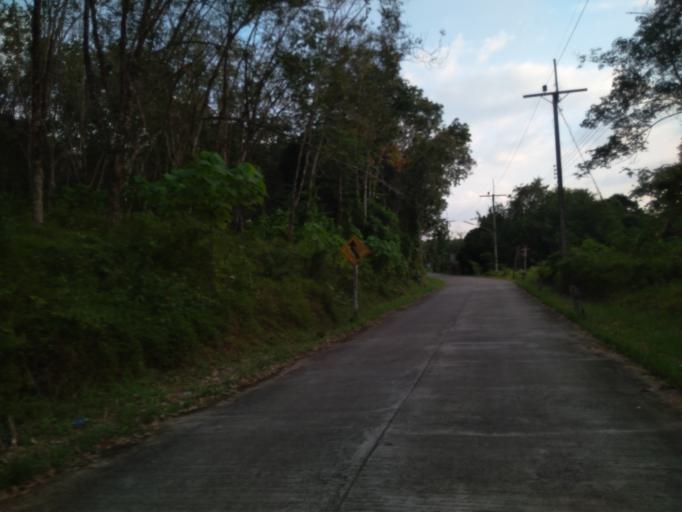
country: TH
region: Phangnga
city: Ko Yao
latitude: 8.1448
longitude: 98.5984
